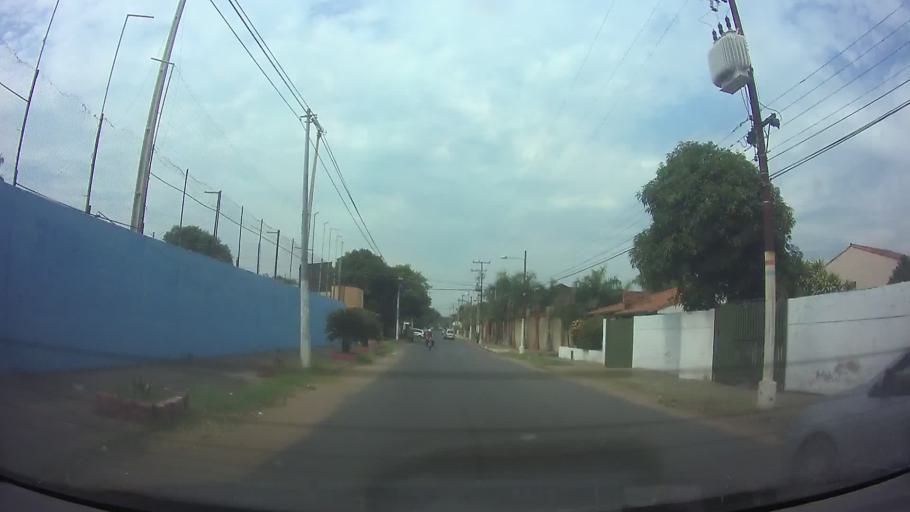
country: PY
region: Central
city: Fernando de la Mora
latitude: -25.2992
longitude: -57.5382
